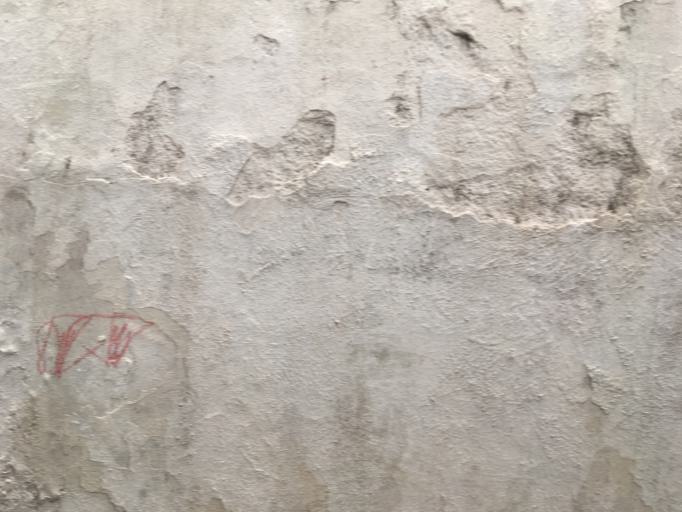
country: BR
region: Rio de Janeiro
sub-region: Rio De Janeiro
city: Rio de Janeiro
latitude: -22.9026
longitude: -43.2445
